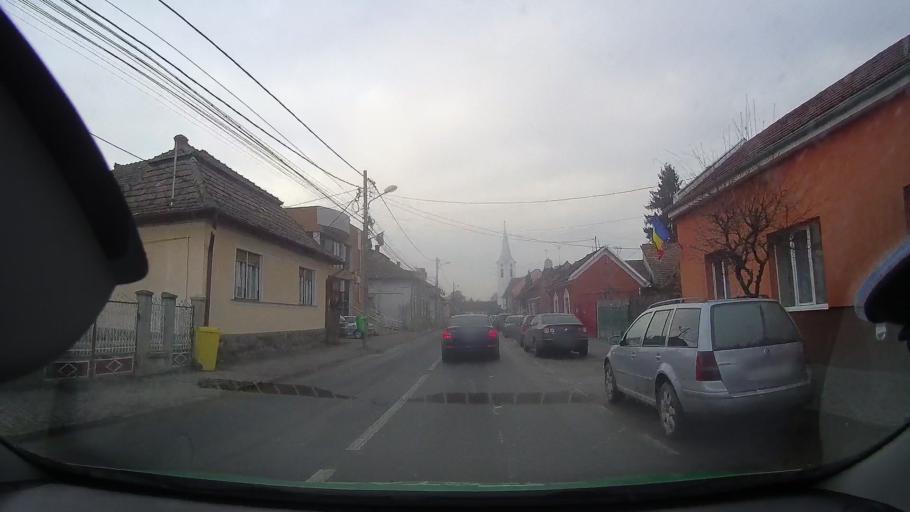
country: RO
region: Mures
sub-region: Comuna Ludus
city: Ludus
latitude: 46.4833
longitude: 24.0957
